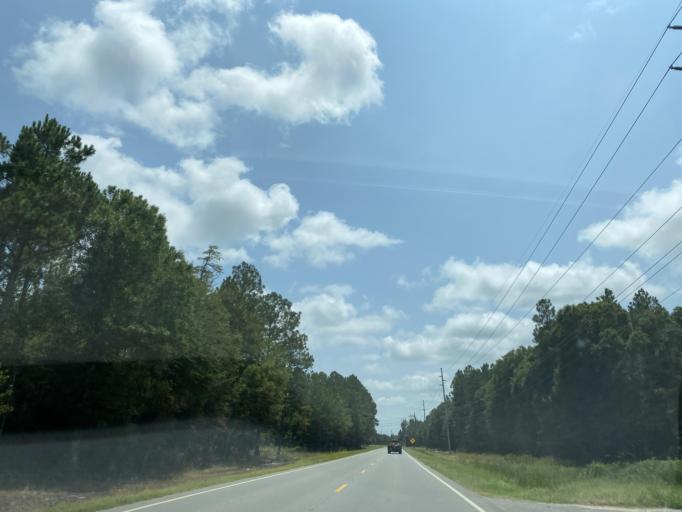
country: US
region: Georgia
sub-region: Jeff Davis County
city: Hazlehurst
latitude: 31.8173
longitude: -82.5678
